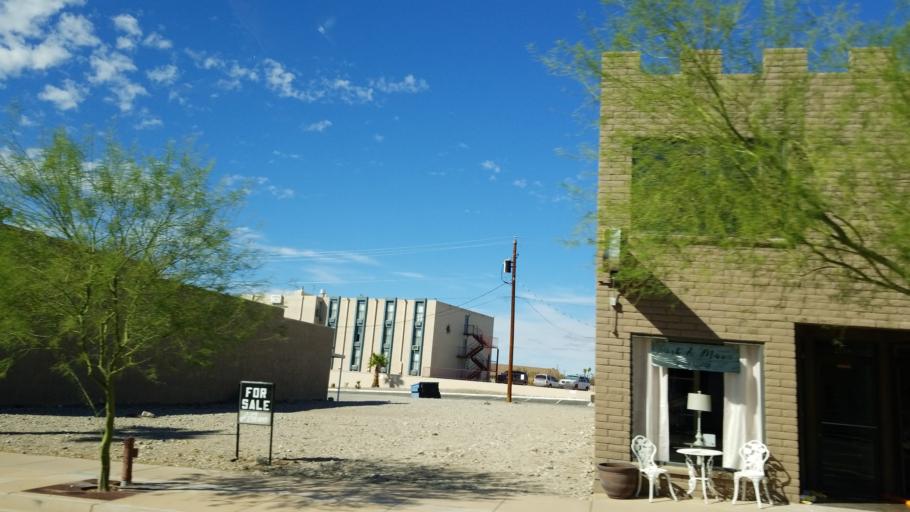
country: US
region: Arizona
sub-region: Mohave County
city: Lake Havasu City
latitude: 34.4749
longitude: -114.3249
